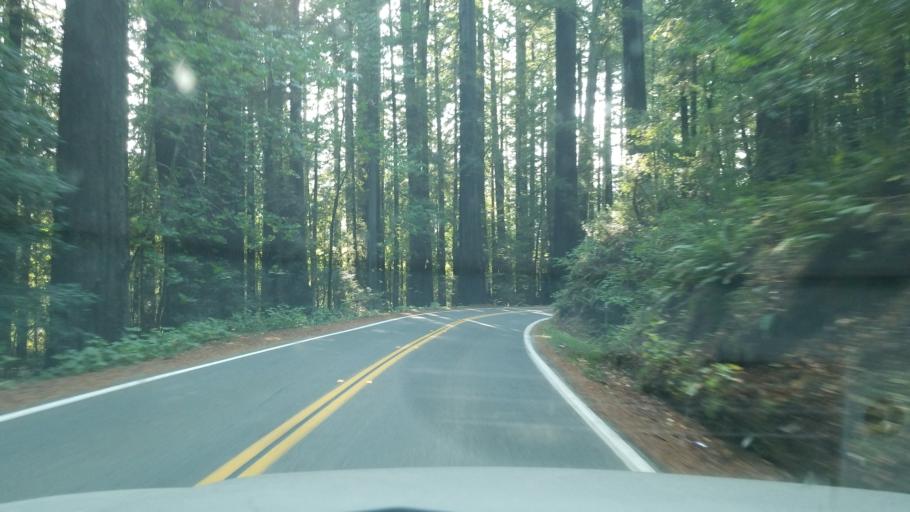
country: US
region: California
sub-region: Humboldt County
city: Redway
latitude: 40.2559
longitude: -123.8223
